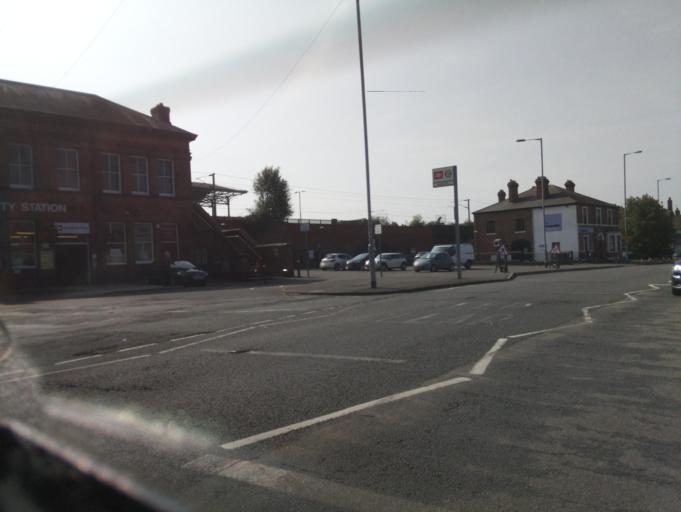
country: GB
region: England
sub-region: Staffordshire
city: Lichfield
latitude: 52.6804
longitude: -1.8260
